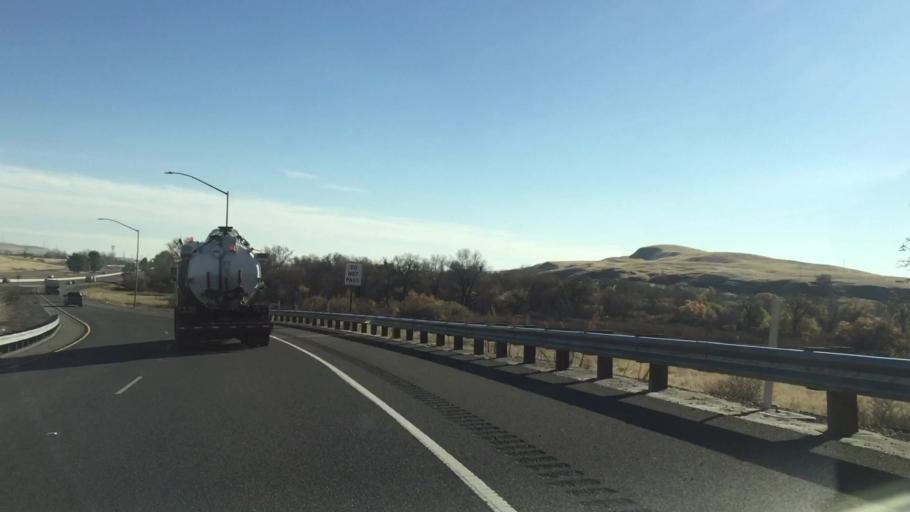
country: US
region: California
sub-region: Butte County
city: Thermalito
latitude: 39.5804
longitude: -121.6221
